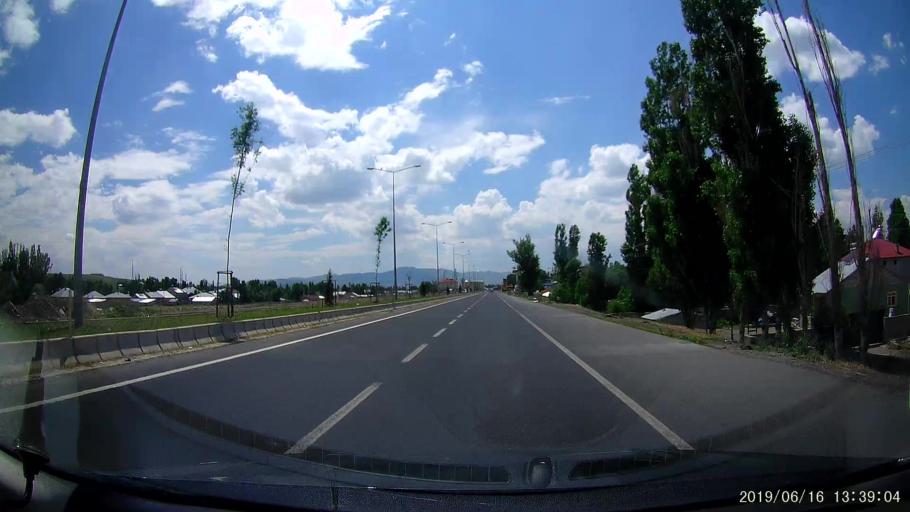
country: TR
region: Agri
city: Agri
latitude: 39.7093
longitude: 43.0640
